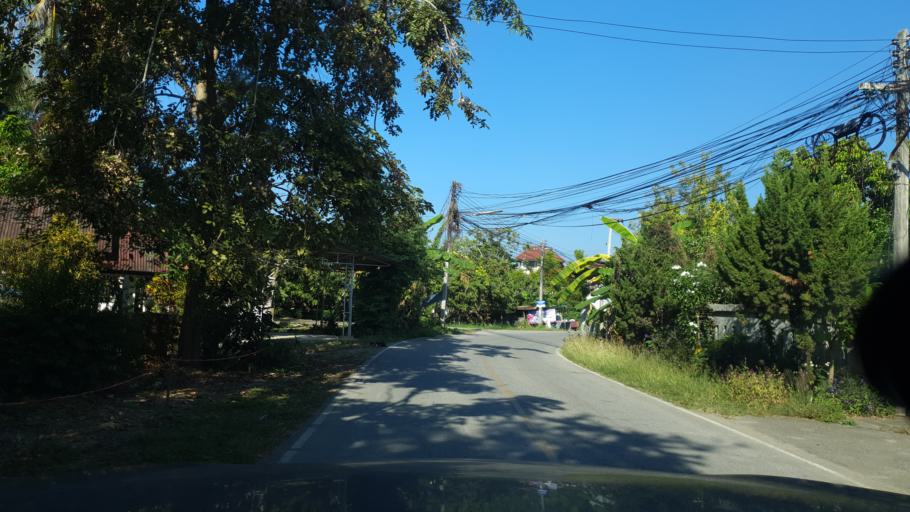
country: TH
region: Chiang Mai
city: Saraphi
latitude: 18.7282
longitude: 99.0631
